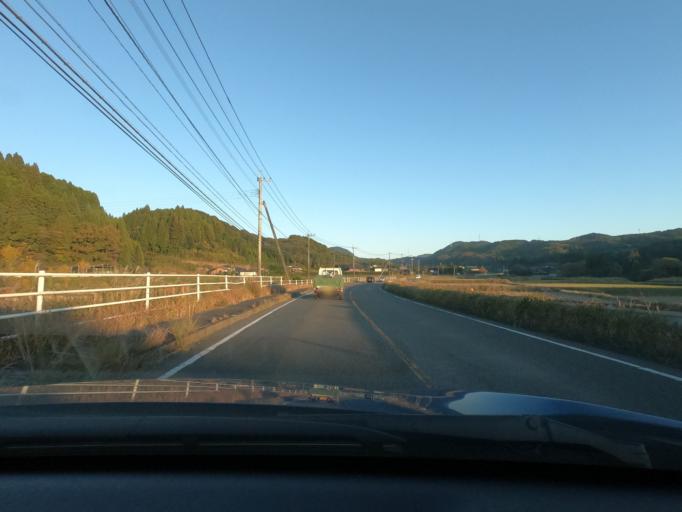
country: JP
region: Kagoshima
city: Satsumasendai
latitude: 31.7940
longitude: 130.4489
